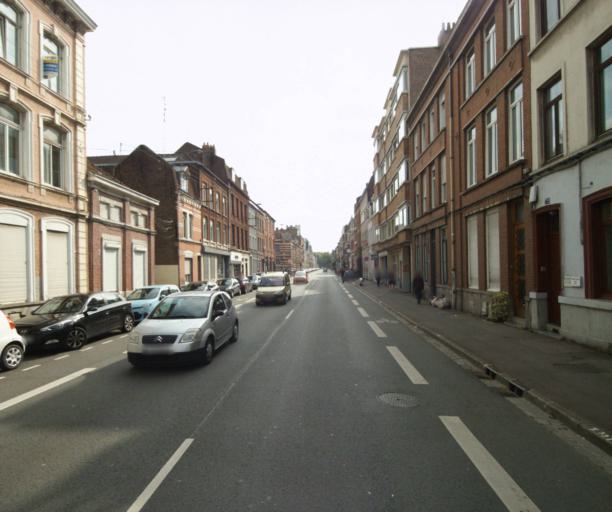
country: FR
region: Nord-Pas-de-Calais
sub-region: Departement du Nord
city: Lille
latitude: 50.6241
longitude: 3.0380
